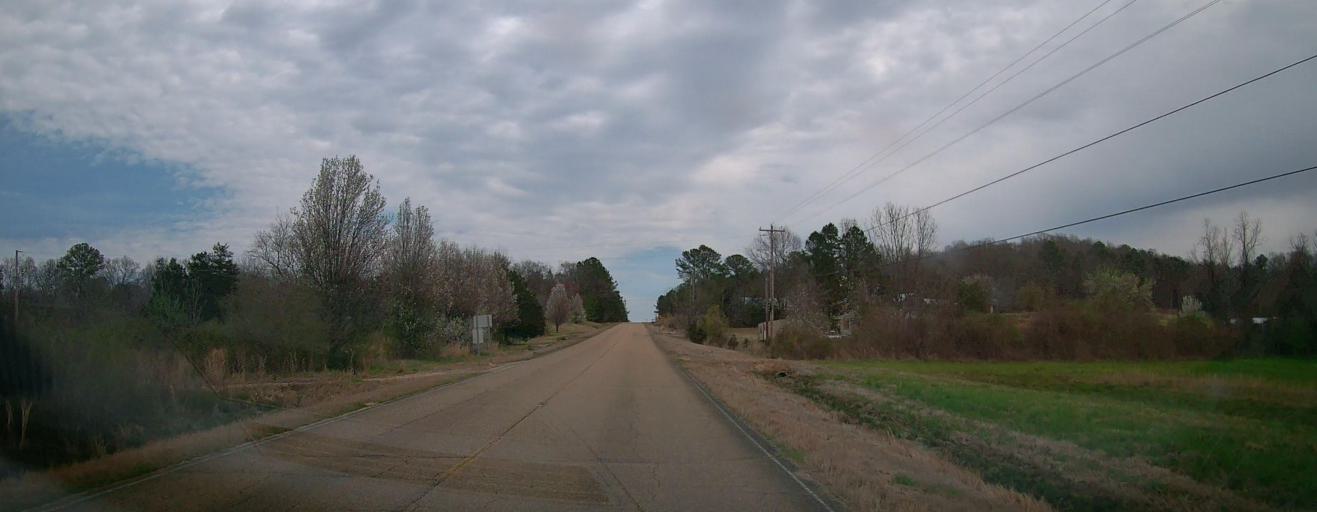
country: US
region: Mississippi
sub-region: Itawamba County
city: Fulton
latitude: 34.2238
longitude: -88.2237
